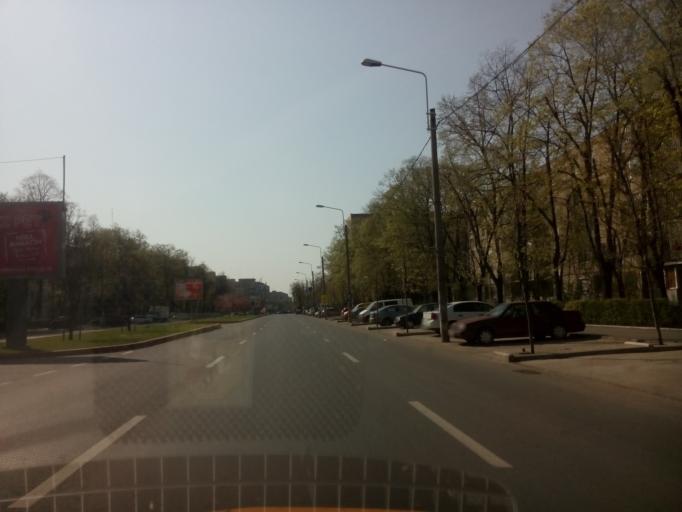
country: RO
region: Ilfov
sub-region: Comuna Fundeni-Dobroesti
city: Fundeni
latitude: 44.4315
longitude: 26.1612
